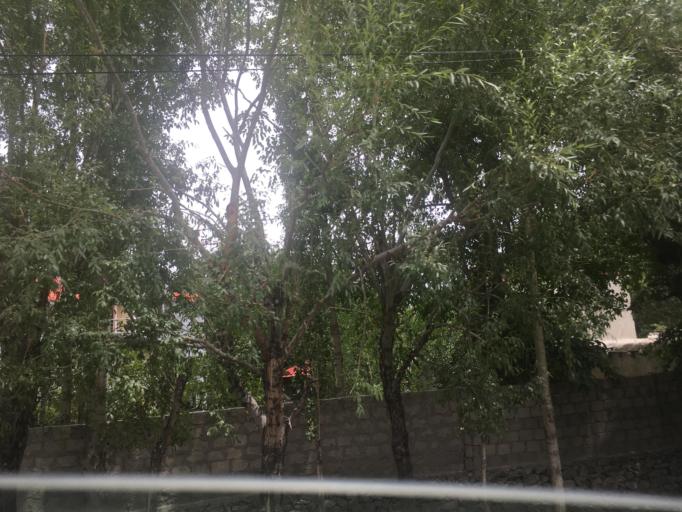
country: PK
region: Gilgit-Baltistan
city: Skardu
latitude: 35.2899
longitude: 75.6436
